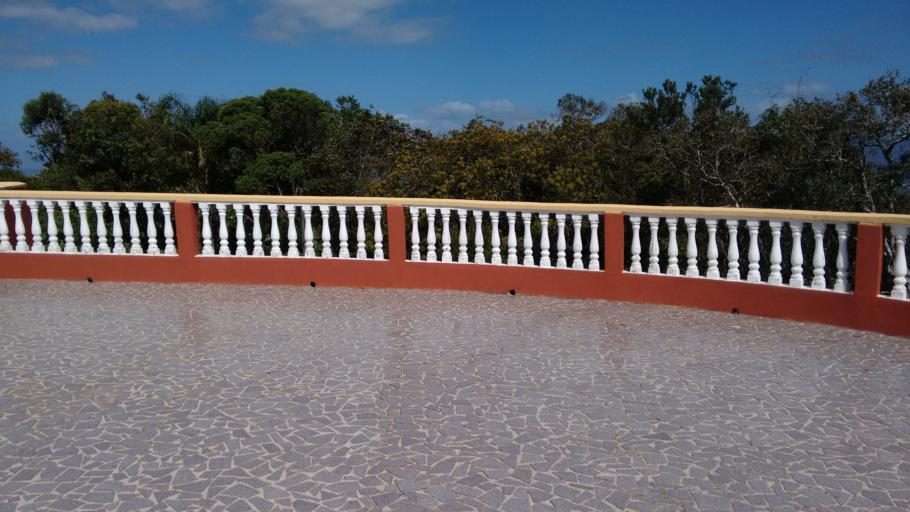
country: BR
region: Santa Catarina
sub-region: Sao Joao Batista
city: Sao Joao Batista
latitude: -27.2657
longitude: -48.9131
